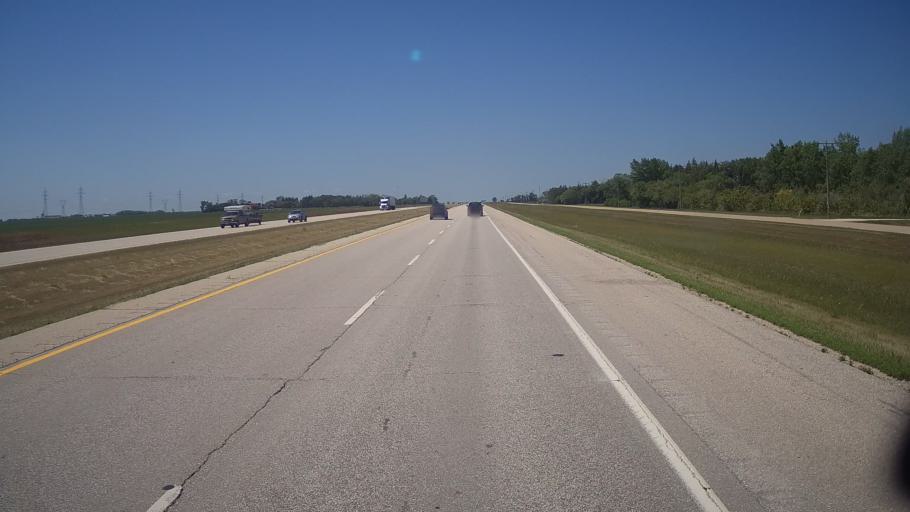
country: CA
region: Manitoba
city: Winnipeg
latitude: 49.9900
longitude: -97.2571
